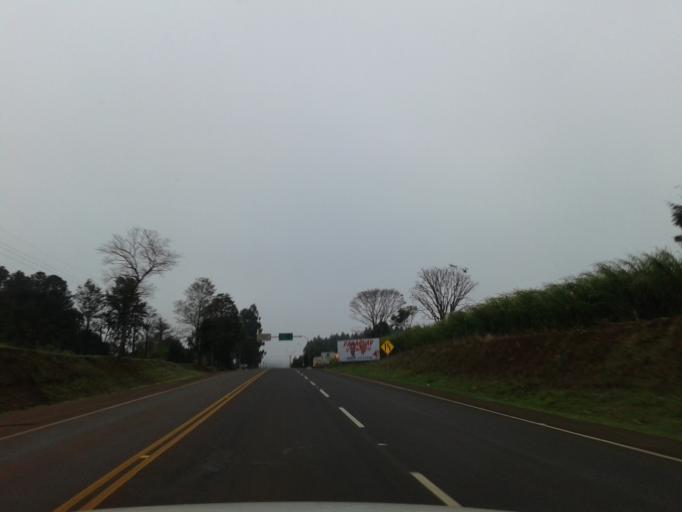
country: PY
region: Itapua
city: Pirapo
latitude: -26.8394
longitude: -55.4221
